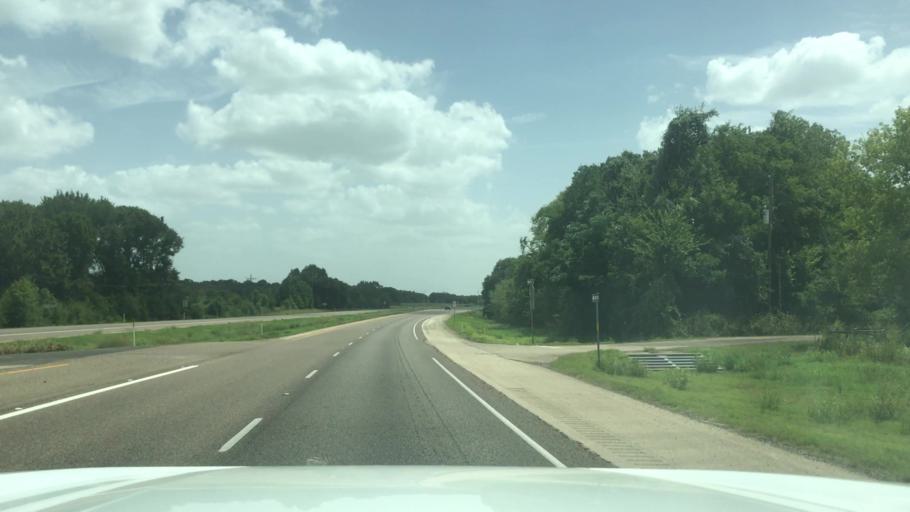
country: US
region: Texas
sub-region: Robertson County
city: Calvert
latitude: 31.1197
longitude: -96.7122
